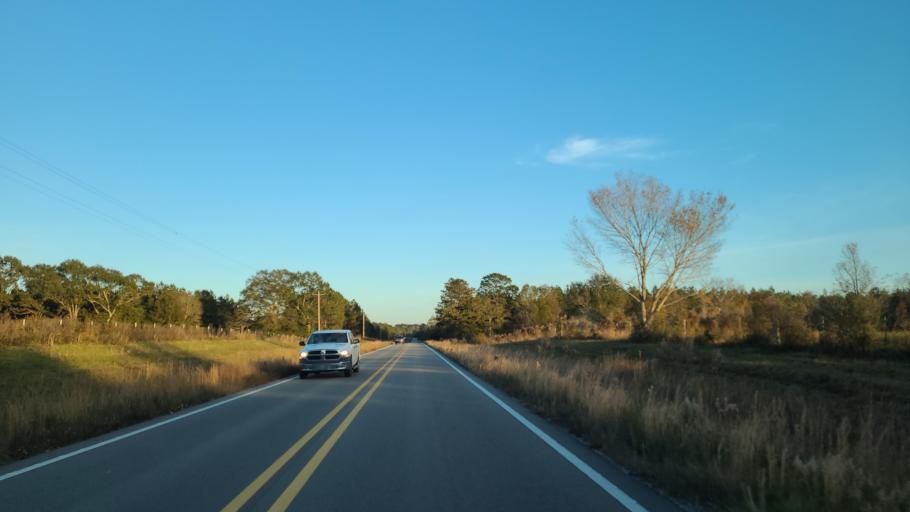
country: US
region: Mississippi
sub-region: Lamar County
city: Lumberton
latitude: 30.9920
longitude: -89.2796
